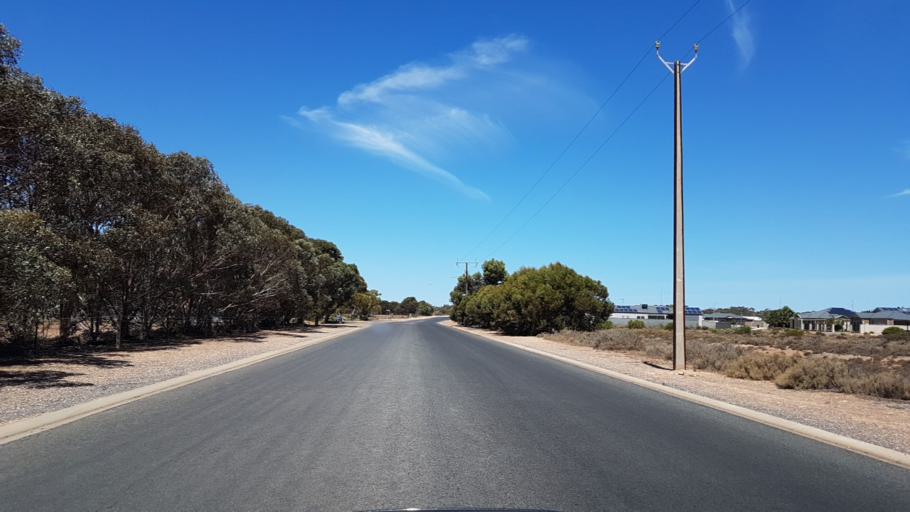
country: AU
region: South Australia
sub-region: Copper Coast
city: Wallaroo
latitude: -34.0534
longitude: 137.5777
